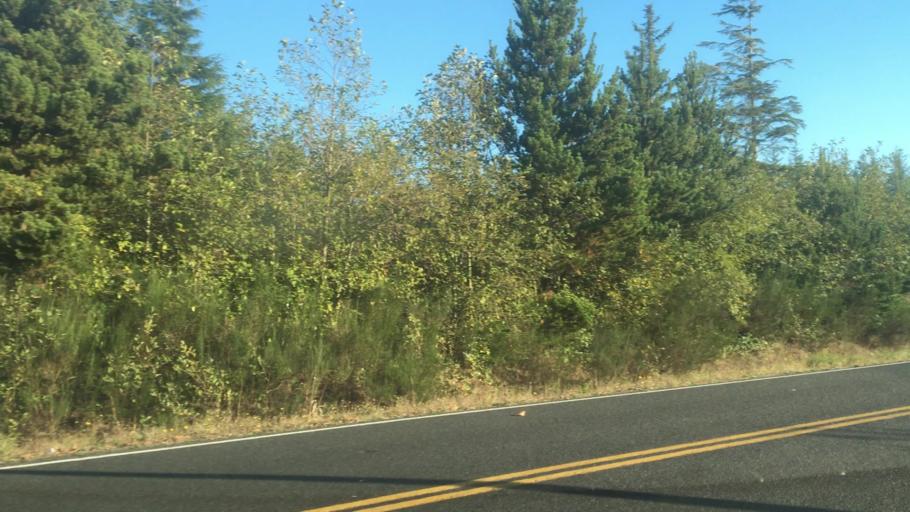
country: US
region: Oregon
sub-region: Clatsop County
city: Warrenton
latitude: 46.1457
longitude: -123.9124
